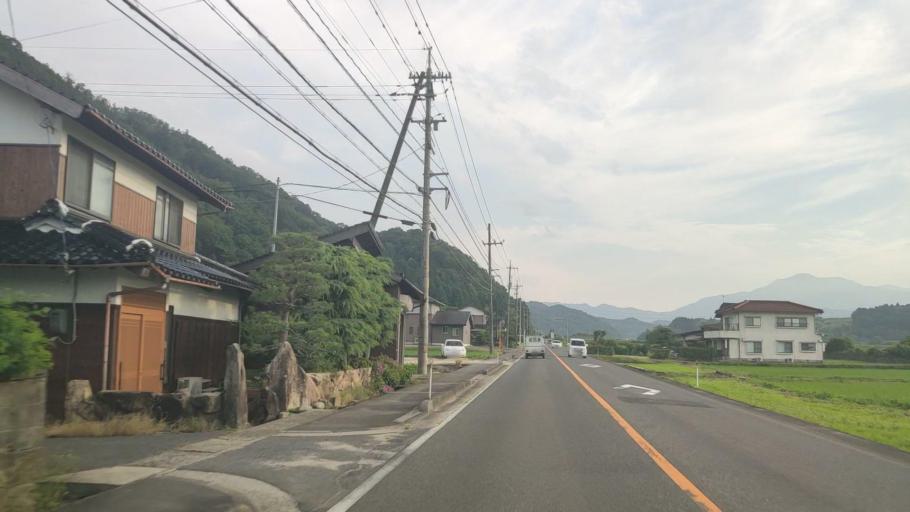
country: JP
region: Tottori
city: Kurayoshi
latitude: 35.3858
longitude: 133.7799
